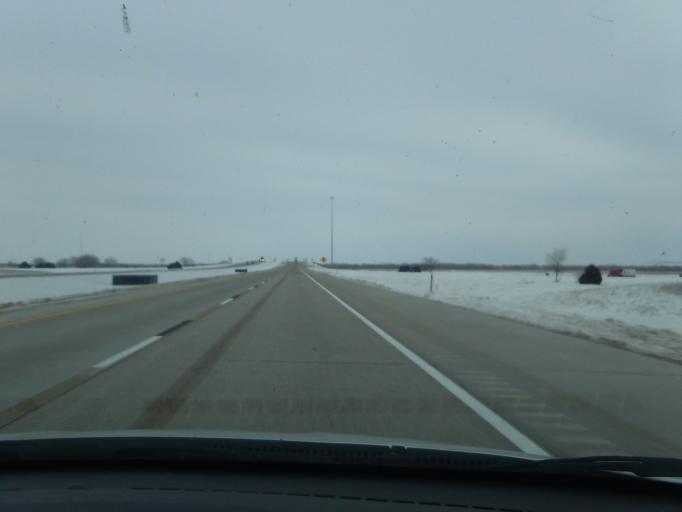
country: US
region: Colorado
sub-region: Sedgwick County
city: Julesburg
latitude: 41.0320
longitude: -102.1891
